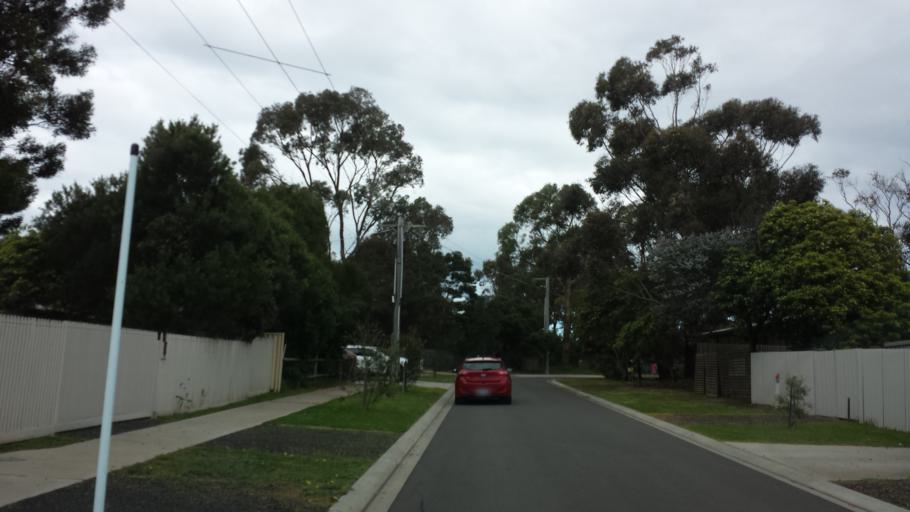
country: AU
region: Victoria
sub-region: Bass Coast
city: Cowes
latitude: -38.4587
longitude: 145.2149
